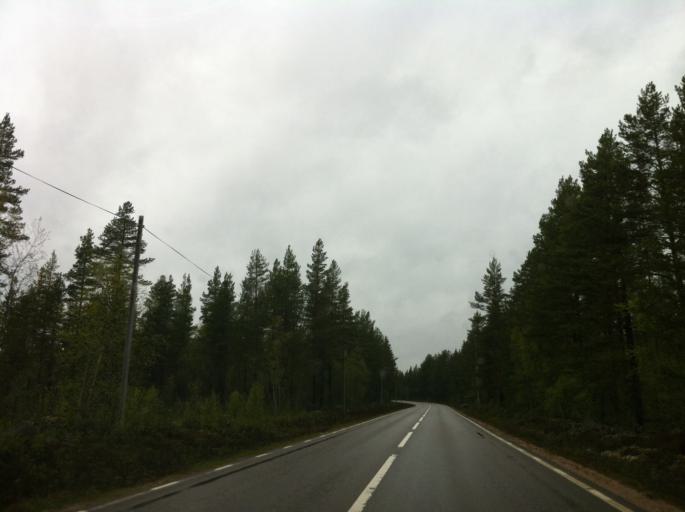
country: SE
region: Jaemtland
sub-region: Harjedalens Kommun
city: Sveg
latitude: 62.1473
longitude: 13.9560
